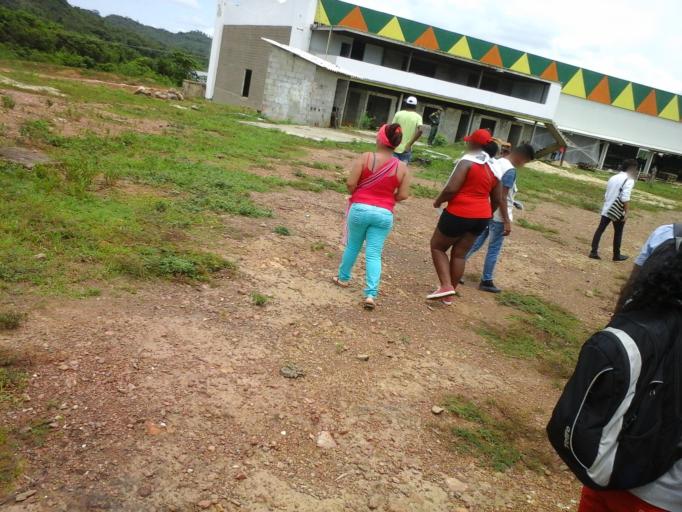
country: CO
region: Bolivar
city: San Cristobal
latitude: 9.8838
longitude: -75.3035
